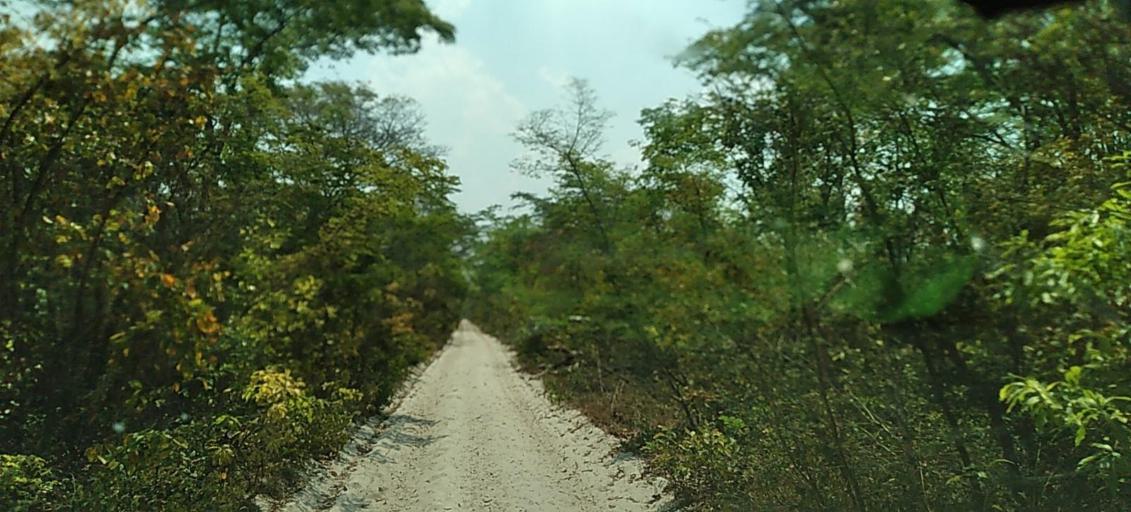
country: ZM
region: North-Western
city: Kabompo
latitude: -13.3953
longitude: 23.7971
